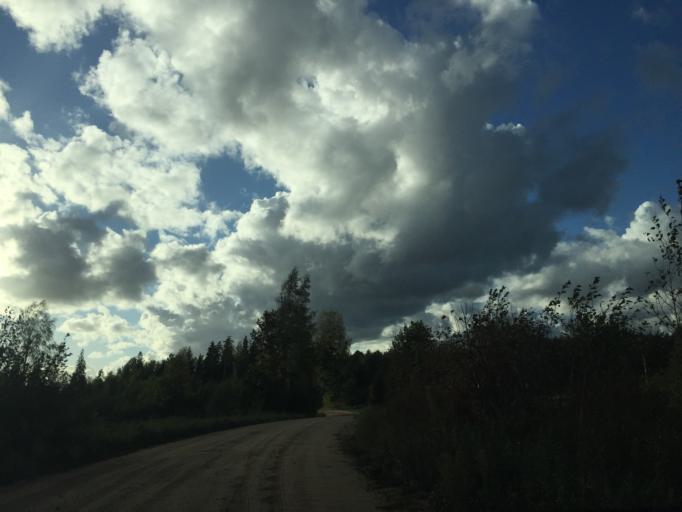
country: LV
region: Ligatne
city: Ligatne
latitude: 57.1309
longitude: 25.1180
